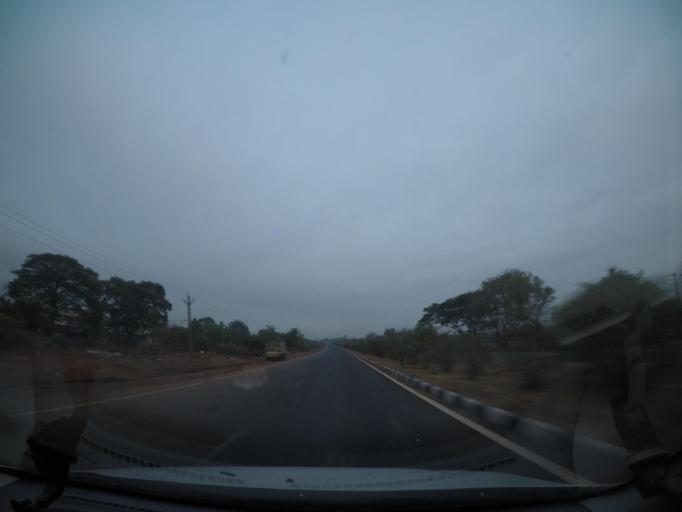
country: IN
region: Andhra Pradesh
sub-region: West Godavari
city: Tadepallegudem
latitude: 16.8092
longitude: 81.3229
